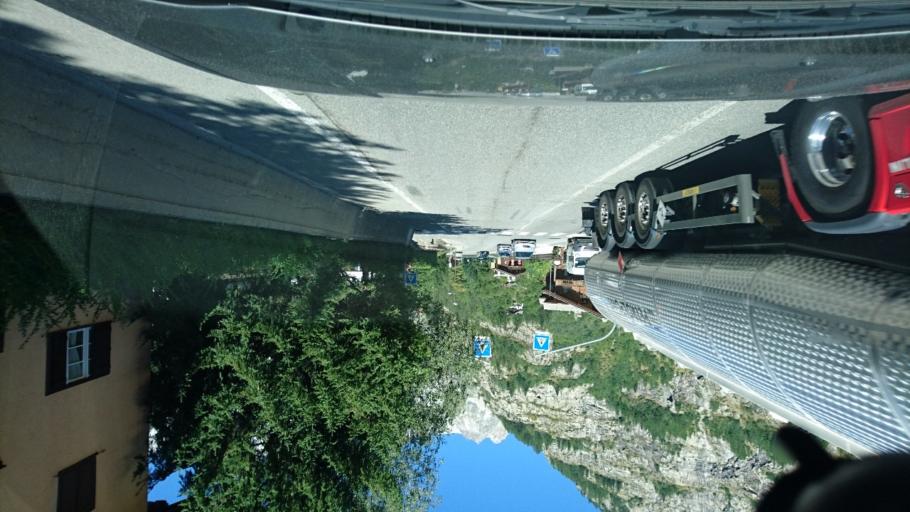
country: IT
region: Aosta Valley
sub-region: Valle d'Aosta
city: Courmayeur
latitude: 45.7933
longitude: 6.9688
